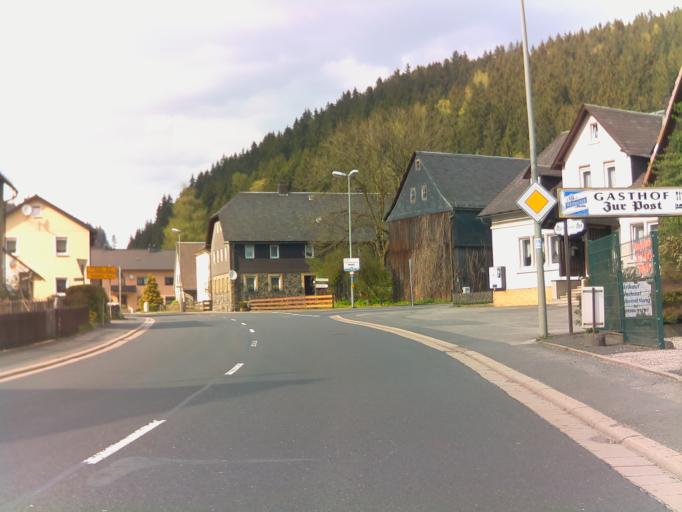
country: DE
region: Bavaria
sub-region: Upper Franconia
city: Teuschnitz
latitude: 50.3916
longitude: 11.3488
